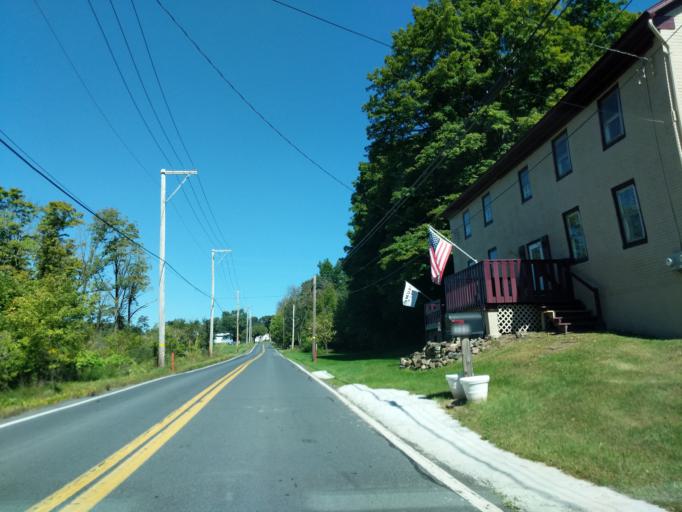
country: US
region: Pennsylvania
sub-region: Bucks County
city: Spinnerstown
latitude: 40.4750
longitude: -75.4663
